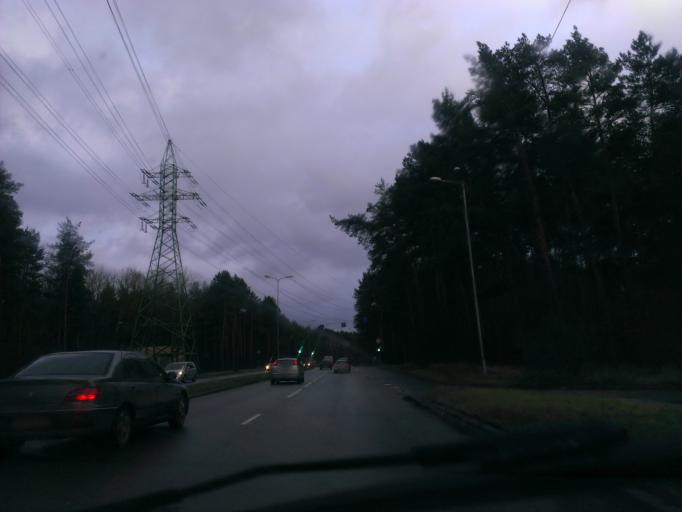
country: LV
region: Riga
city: Jaunciems
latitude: 56.9671
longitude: 24.1970
